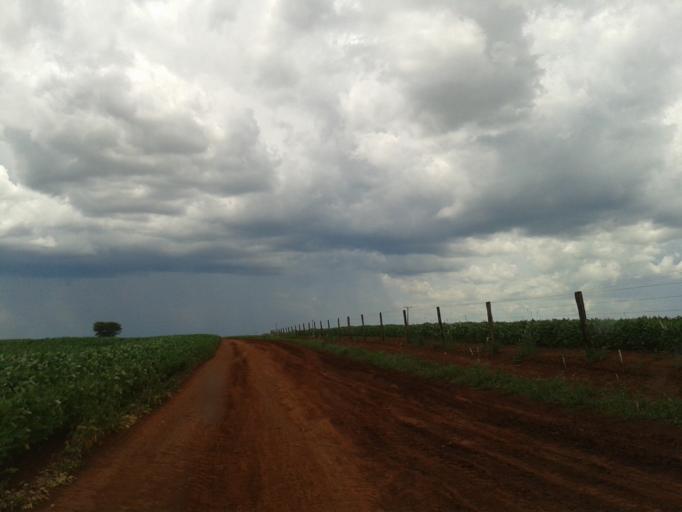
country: BR
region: Minas Gerais
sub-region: Centralina
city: Centralina
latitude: -18.7019
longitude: -49.2170
